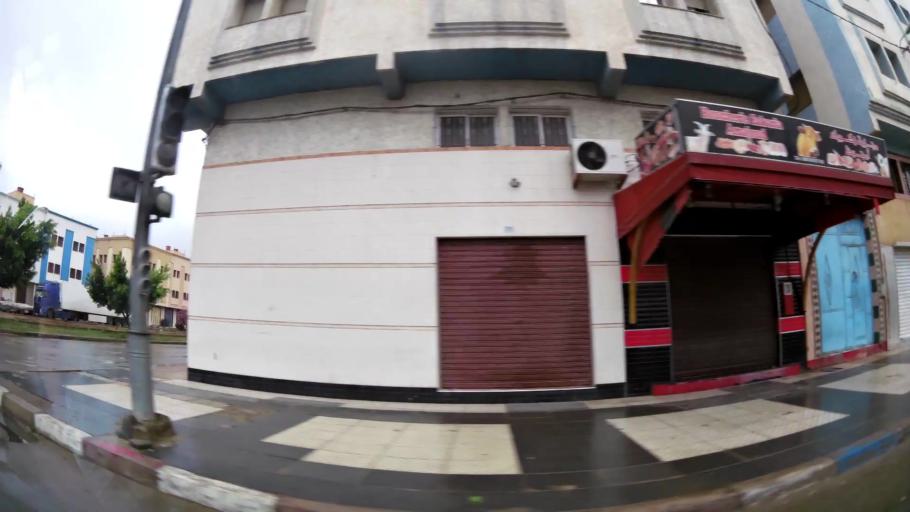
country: MA
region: Oriental
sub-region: Nador
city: Nador
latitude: 35.1648
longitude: -2.9564
